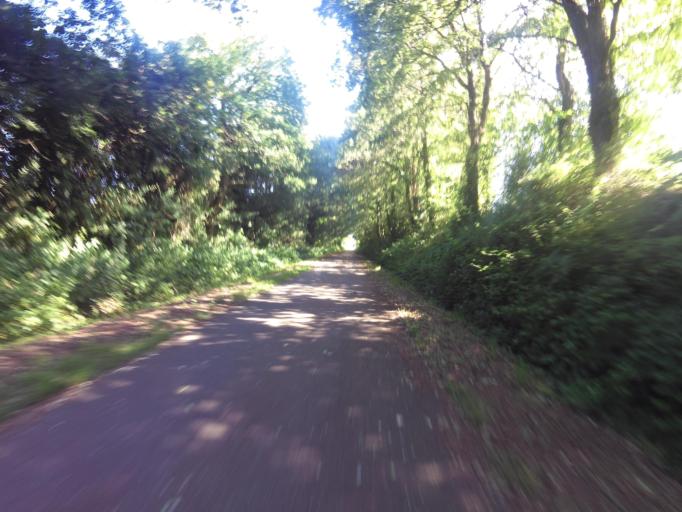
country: FR
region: Brittany
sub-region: Departement du Morbihan
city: Guillac
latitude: 47.8815
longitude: -2.4368
